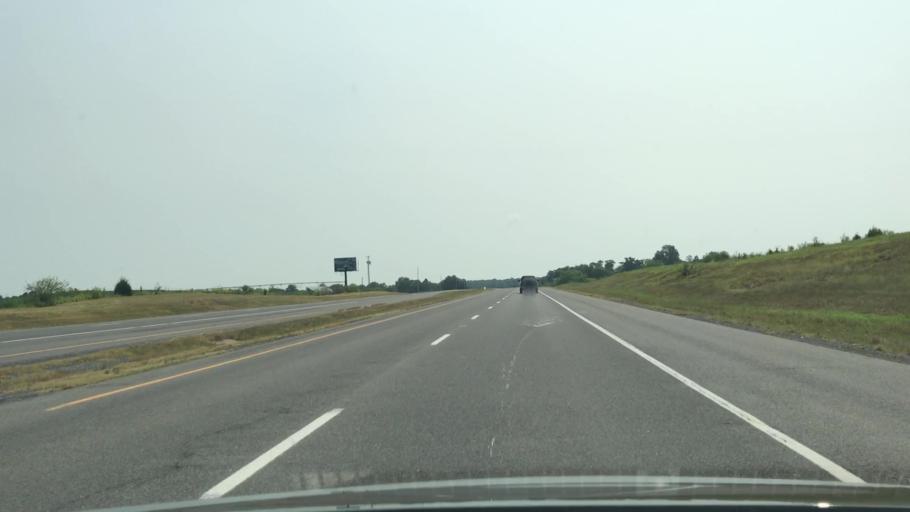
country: US
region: Kentucky
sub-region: Calloway County
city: Murray
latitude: 36.6497
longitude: -88.2578
